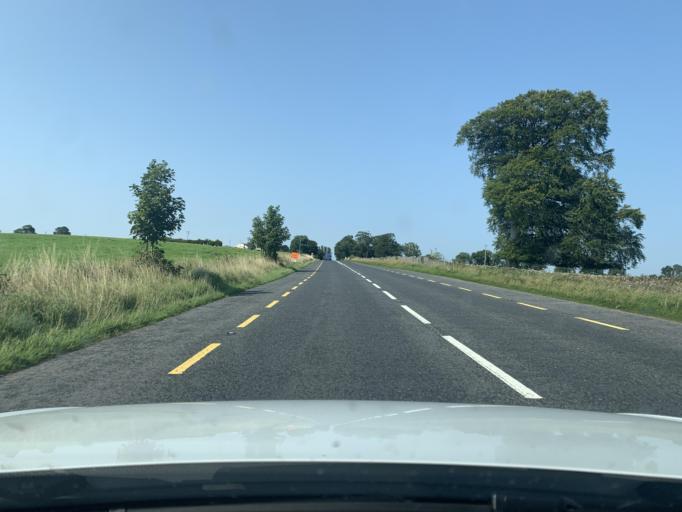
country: IE
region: Leinster
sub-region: An Iarmhi
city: Athlone
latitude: 53.4959
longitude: -8.0366
